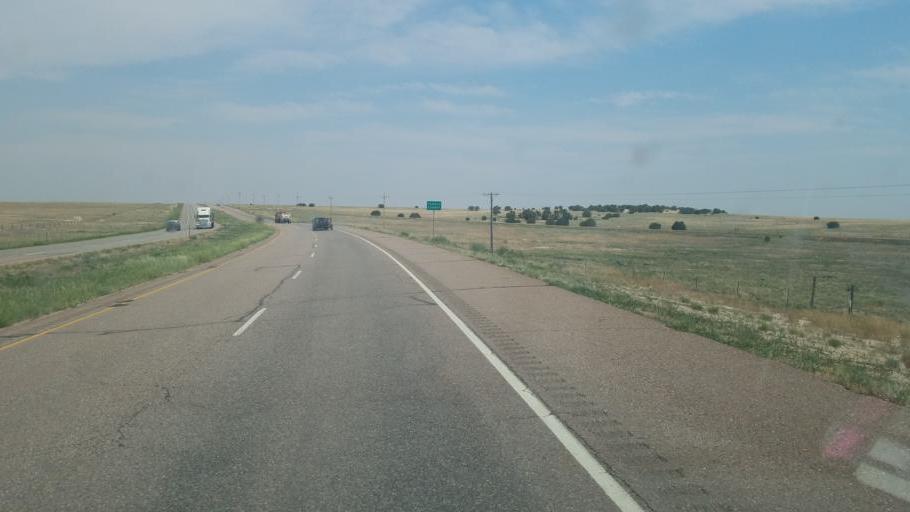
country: US
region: Colorado
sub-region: Fremont County
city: Penrose
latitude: 38.3725
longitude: -104.9417
